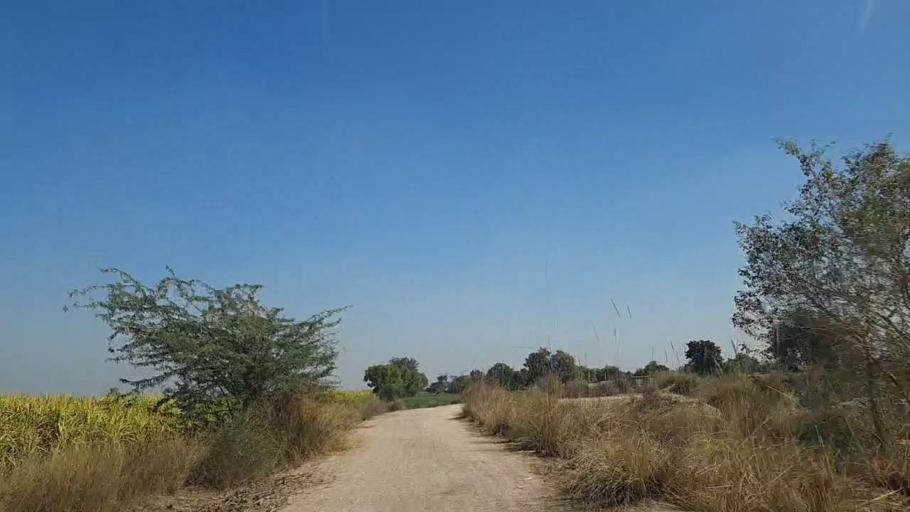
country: PK
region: Sindh
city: Sakrand
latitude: 26.2458
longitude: 68.1994
